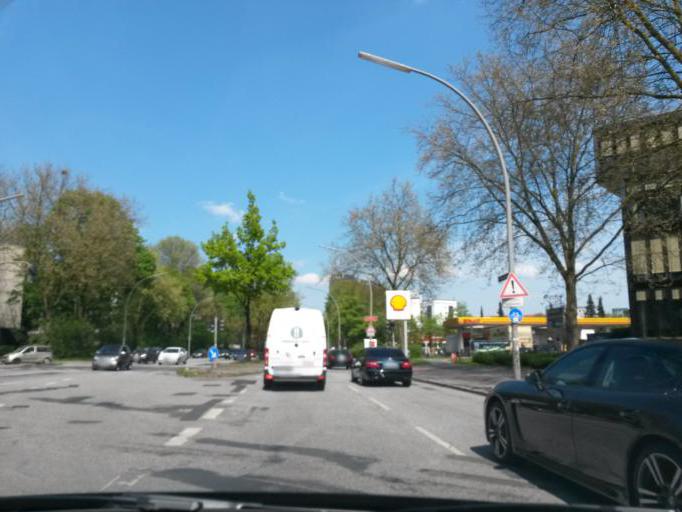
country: DE
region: Hamburg
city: St. Pauli
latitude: 53.5669
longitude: 9.9520
